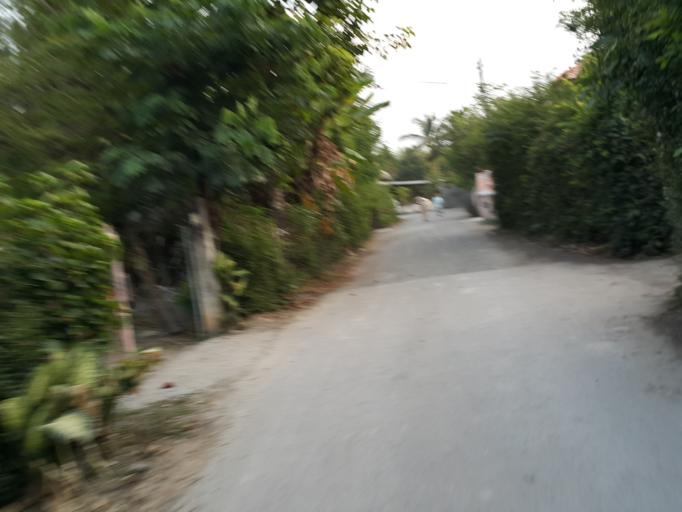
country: TH
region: Chiang Mai
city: San Sai
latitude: 18.8327
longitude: 99.1089
